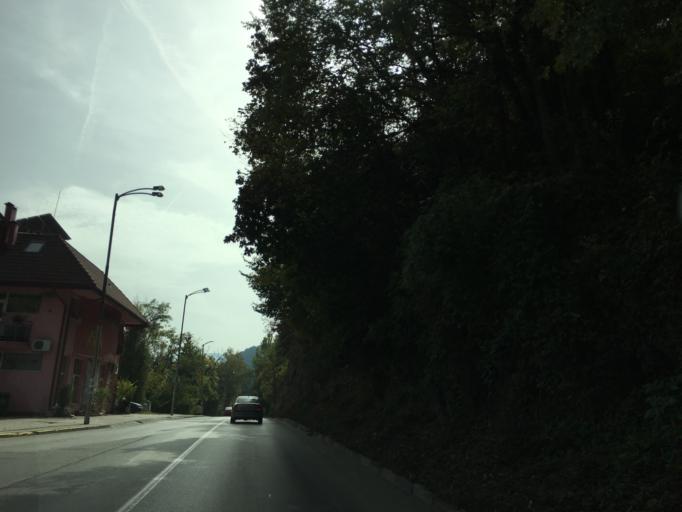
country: BG
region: Sofia-Capital
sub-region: Stolichna Obshtina
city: Sofia
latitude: 42.6027
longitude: 23.4027
